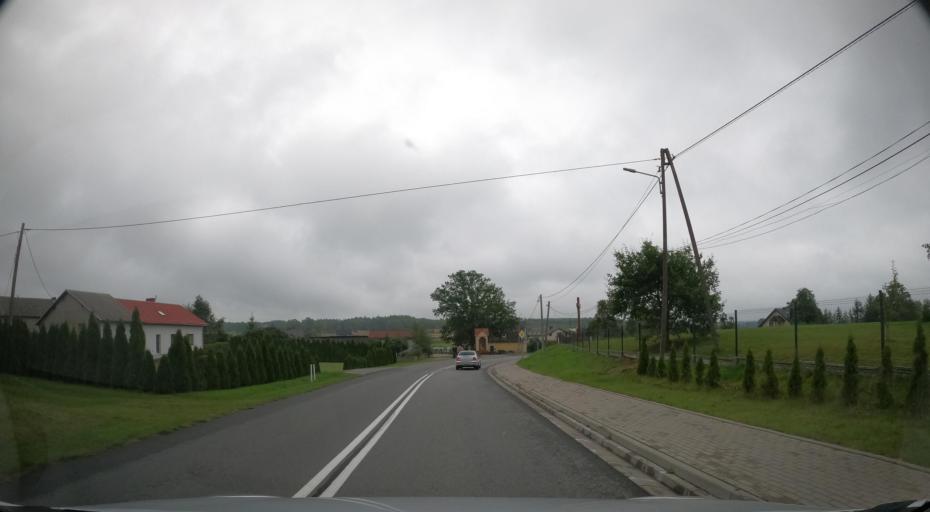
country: PL
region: Pomeranian Voivodeship
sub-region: Powiat wejherowski
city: Linia
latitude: 54.4803
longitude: 17.8553
